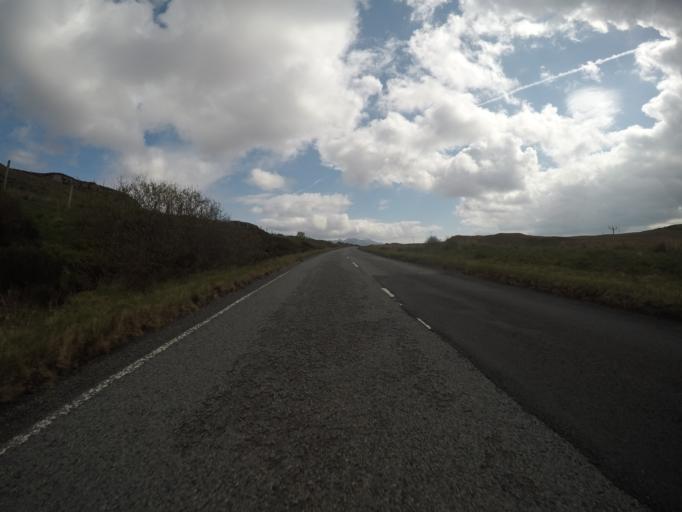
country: GB
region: Scotland
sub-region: Highland
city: Isle of Skye
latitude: 57.3192
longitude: -6.3232
